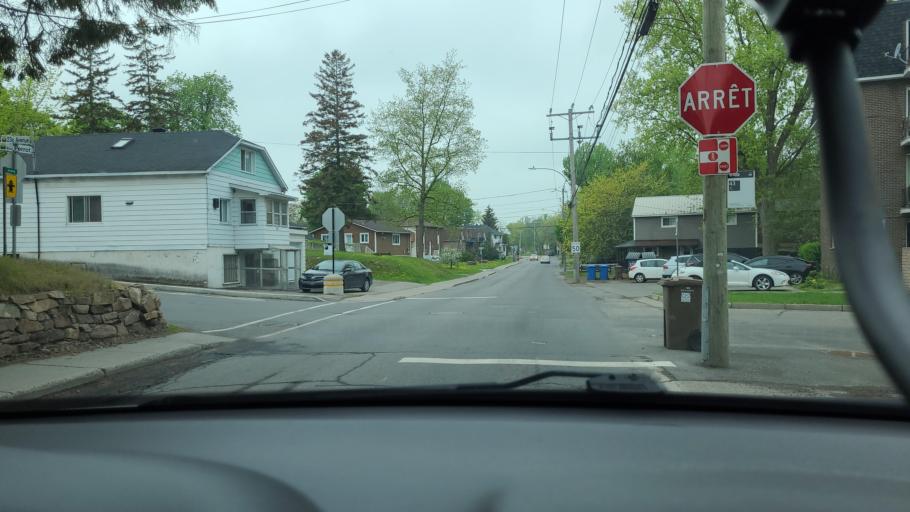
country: CA
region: Quebec
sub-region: Monteregie
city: L'Ile-Perrot
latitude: 45.3932
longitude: -73.9482
